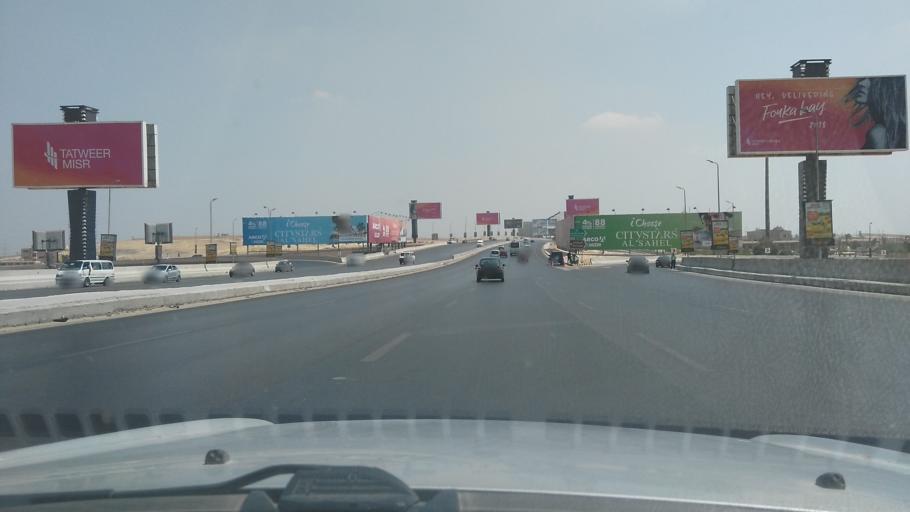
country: EG
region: Al Jizah
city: Awsim
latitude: 30.0475
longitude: 31.0529
